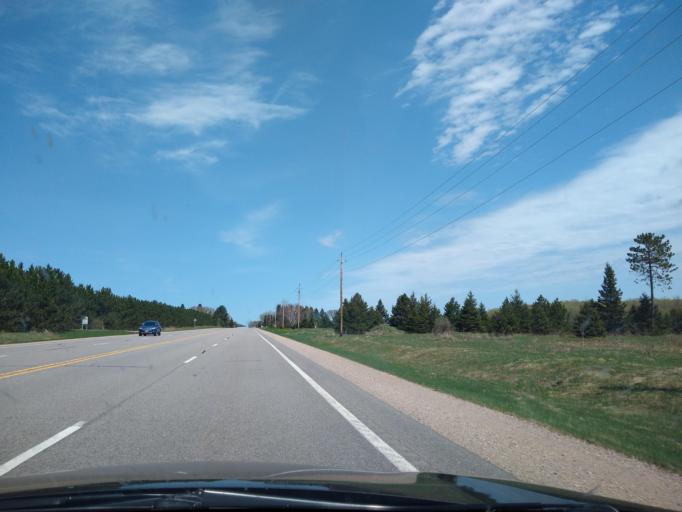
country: US
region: Michigan
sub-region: Delta County
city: Gladstone
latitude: 46.0805
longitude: -86.9808
